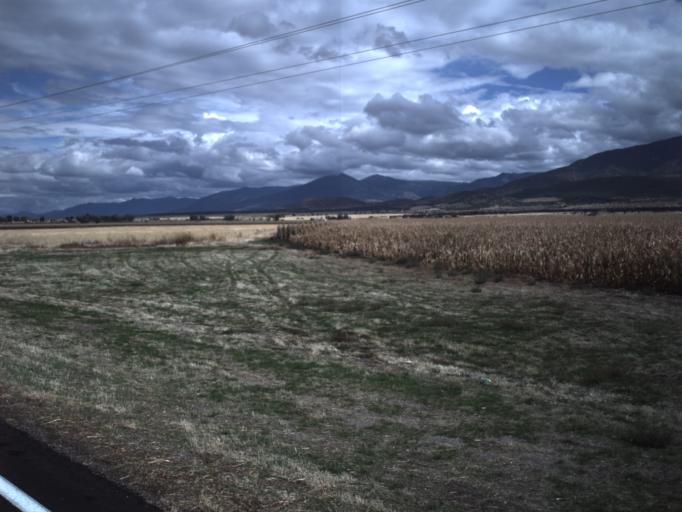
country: US
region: Utah
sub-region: Millard County
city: Fillmore
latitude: 38.8645
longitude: -112.4174
